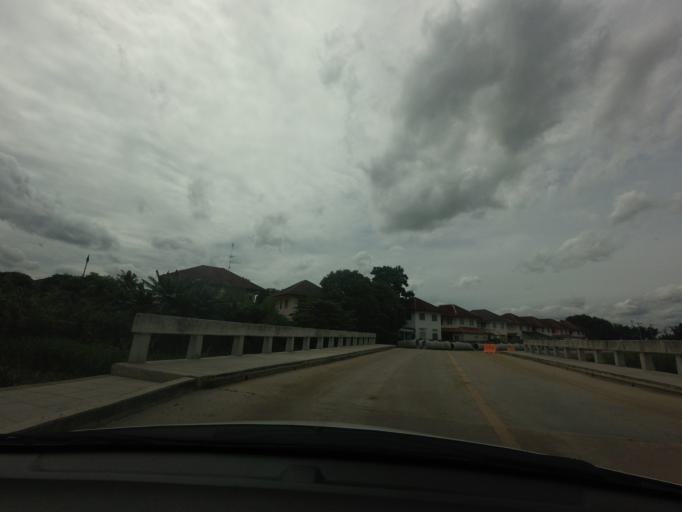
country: TH
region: Bangkok
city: Min Buri
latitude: 13.7780
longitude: 100.7616
